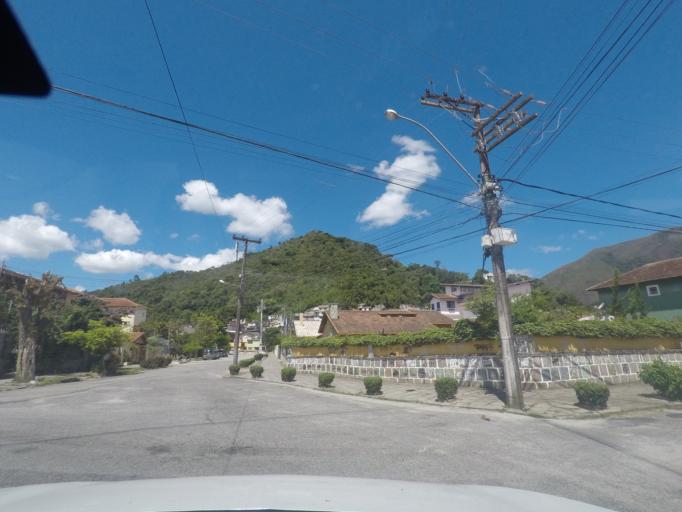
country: BR
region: Rio de Janeiro
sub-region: Teresopolis
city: Teresopolis
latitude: -22.4311
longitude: -42.9778
